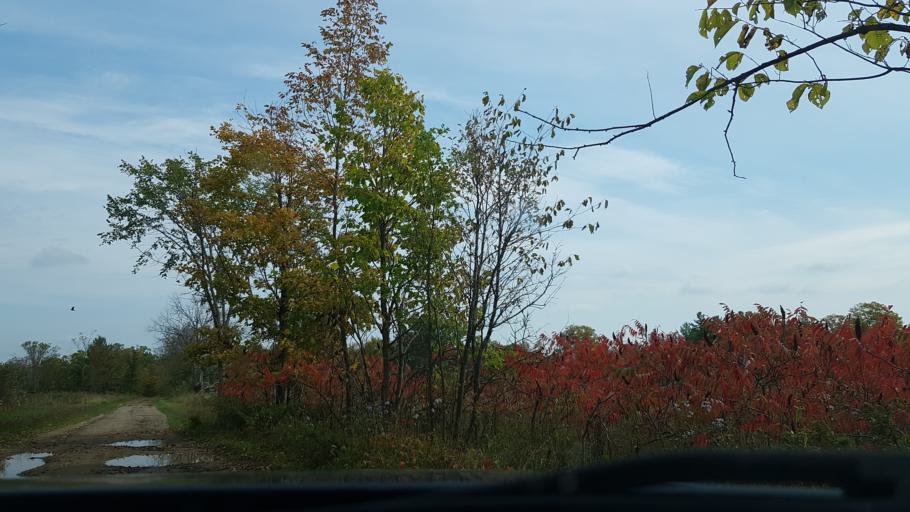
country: CA
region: Ontario
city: Orillia
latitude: 44.6907
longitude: -79.0285
